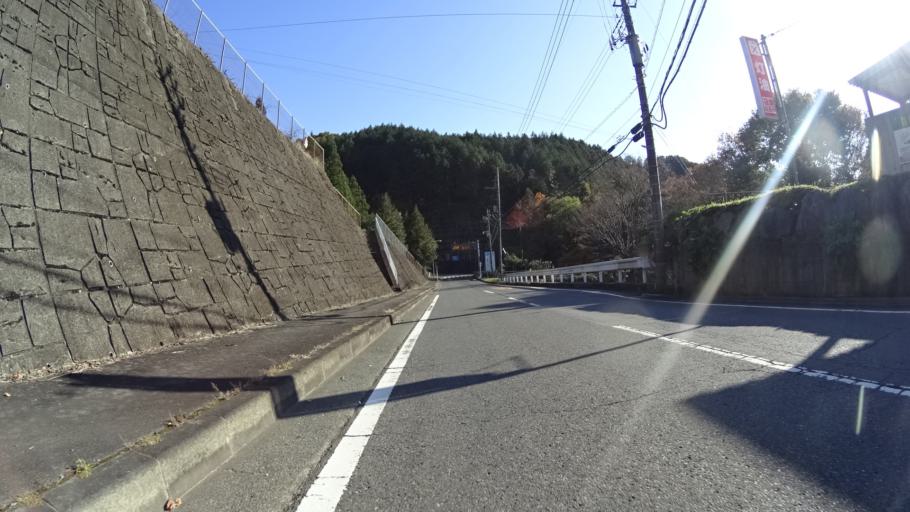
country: JP
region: Yamanashi
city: Uenohara
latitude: 35.6419
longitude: 139.1278
